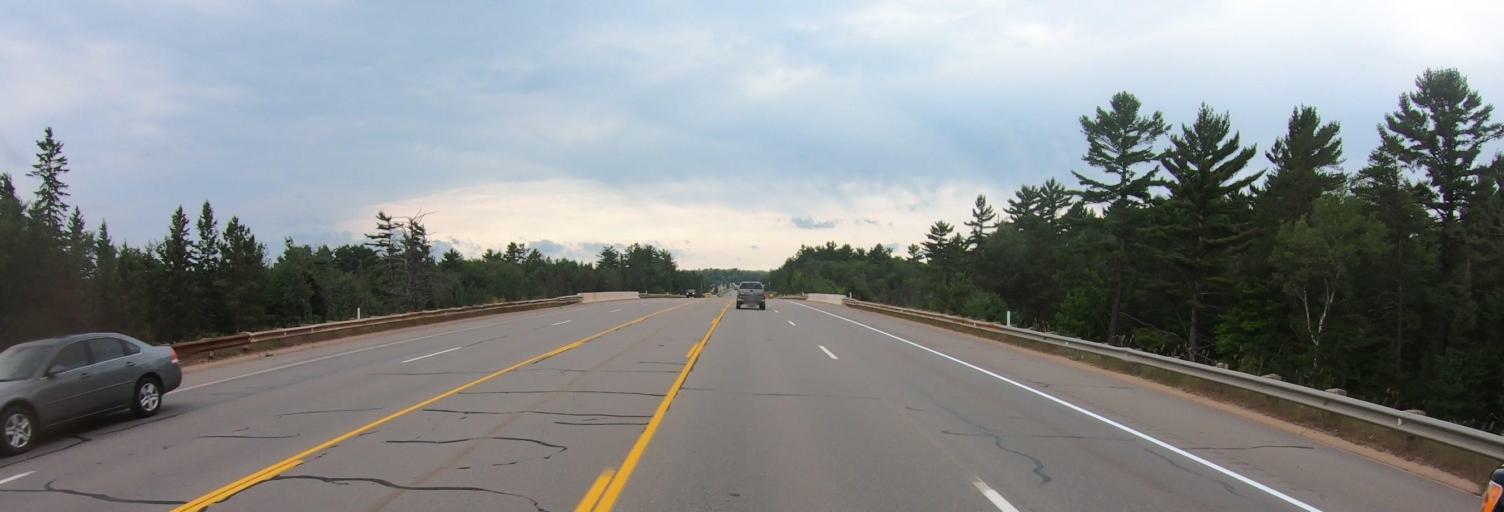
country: US
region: Michigan
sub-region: Marquette County
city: West Ishpeming
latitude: 46.4910
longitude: -87.7026
